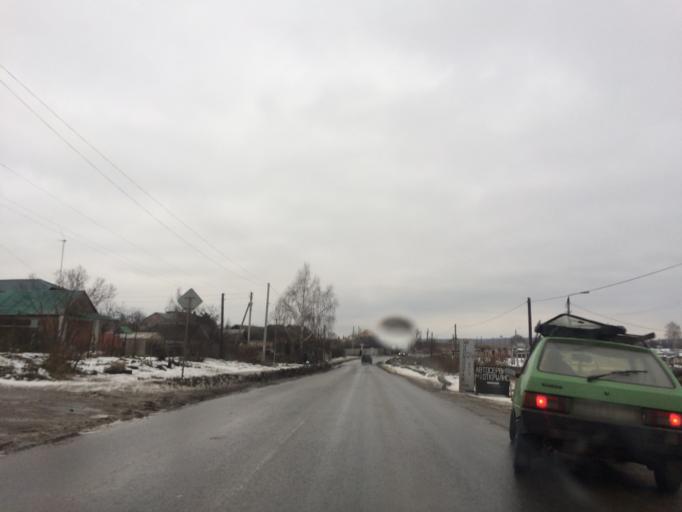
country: RU
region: Tula
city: Tula
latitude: 54.1888
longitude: 37.7185
